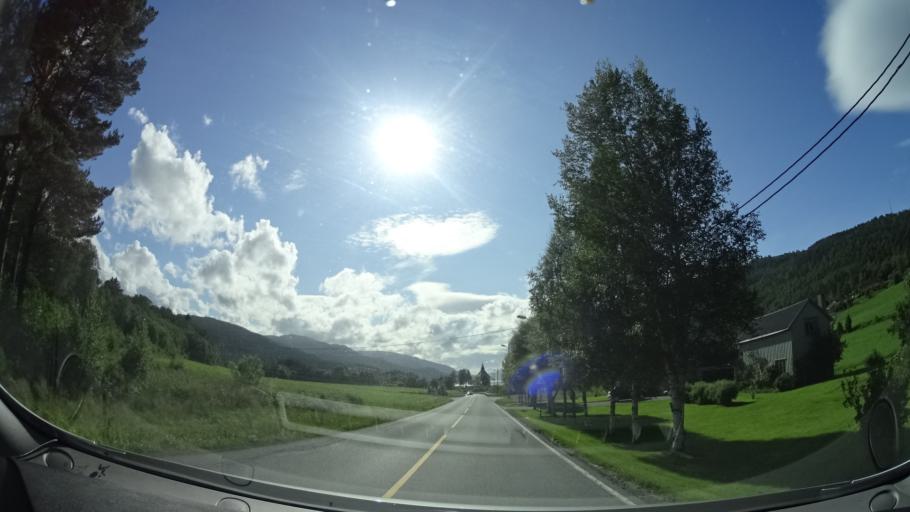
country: NO
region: Sor-Trondelag
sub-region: Hemne
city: Kyrksaeterora
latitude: 63.2069
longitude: 9.0053
